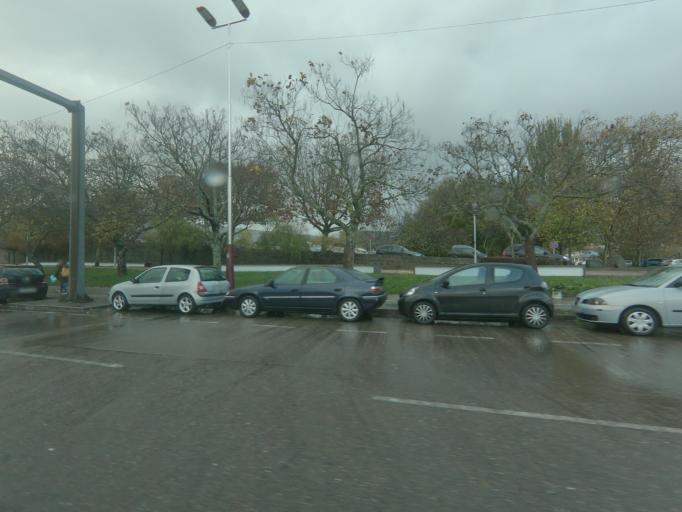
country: ES
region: Galicia
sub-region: Provincia de Pontevedra
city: Pontevedra
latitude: 42.4356
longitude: -8.6413
